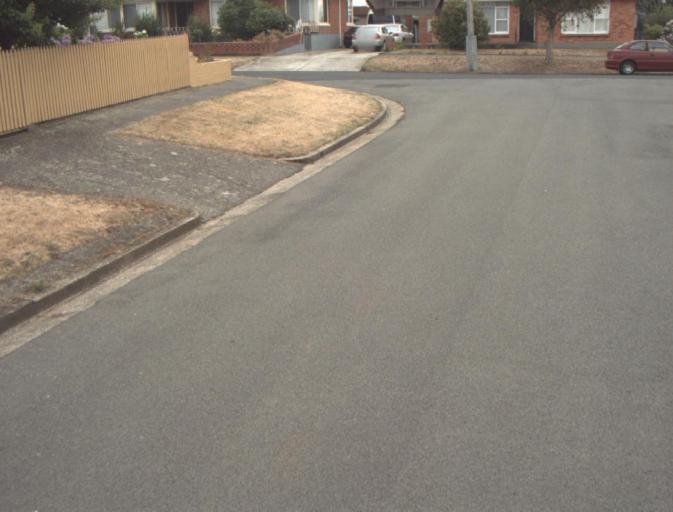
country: AU
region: Tasmania
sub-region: Launceston
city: East Launceston
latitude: -41.4757
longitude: 147.1694
